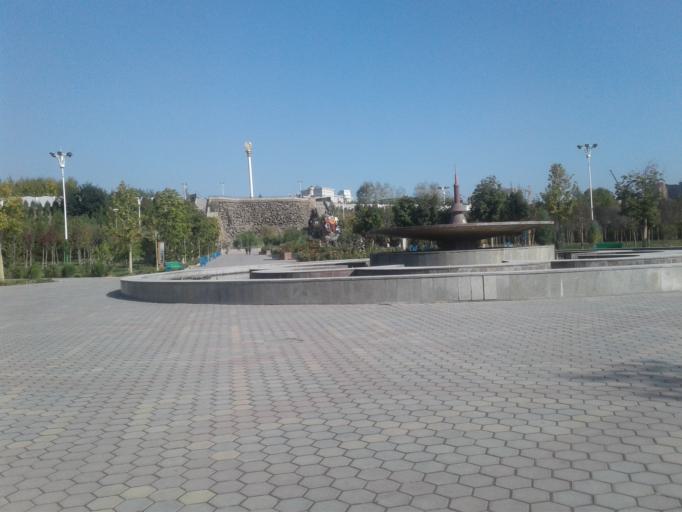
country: TJ
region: Dushanbe
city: Dushanbe
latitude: 38.5741
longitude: 68.7750
